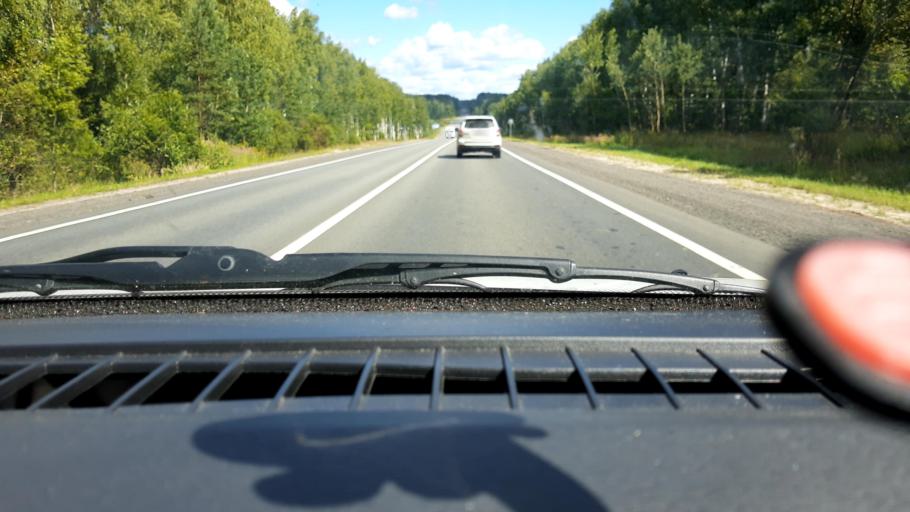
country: RU
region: Nizjnij Novgorod
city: Arzamas
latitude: 55.4925
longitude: 43.8900
